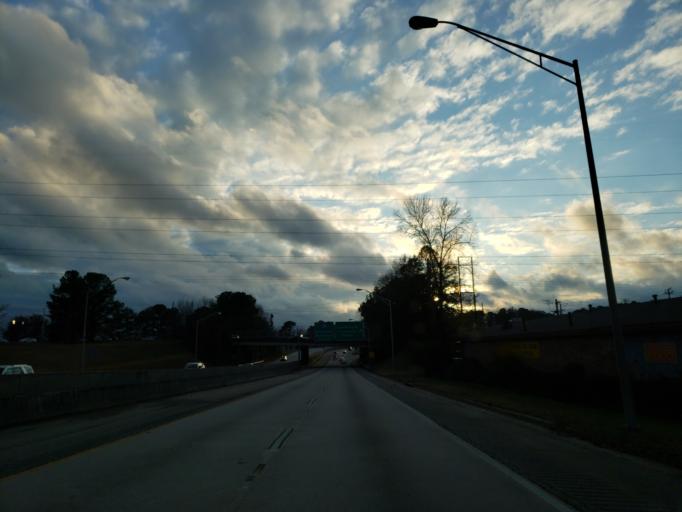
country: US
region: Georgia
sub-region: Fulton County
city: East Point
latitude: 33.6931
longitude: -84.4890
